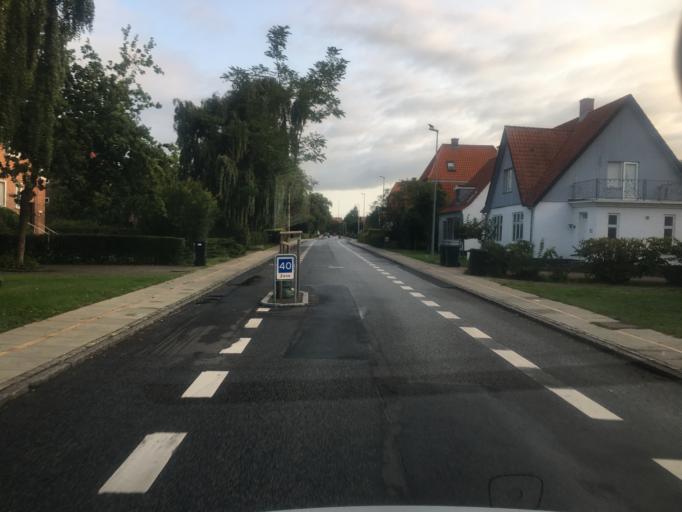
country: DK
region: South Denmark
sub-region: Tonder Kommune
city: Tonder
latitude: 54.9396
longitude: 8.8656
